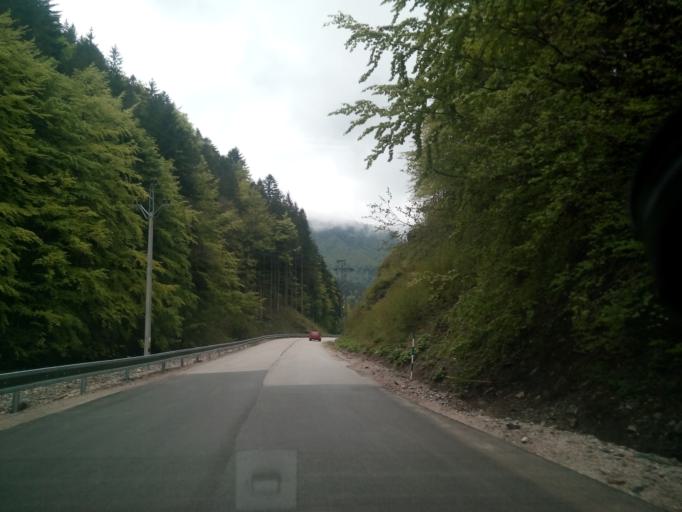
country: SK
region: Zilinsky
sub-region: Okres Zilina
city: Terchova
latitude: 49.2145
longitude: 19.0374
